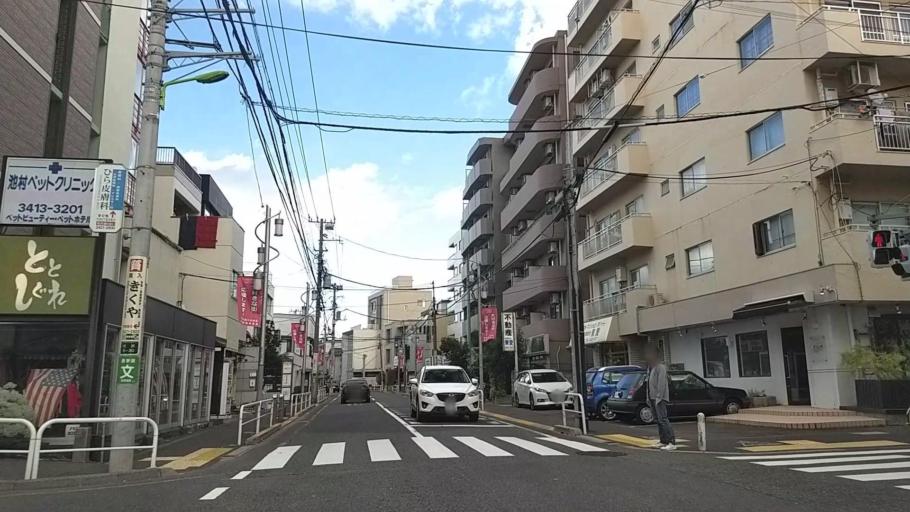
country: JP
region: Tokyo
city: Tokyo
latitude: 35.6577
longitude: 139.6678
